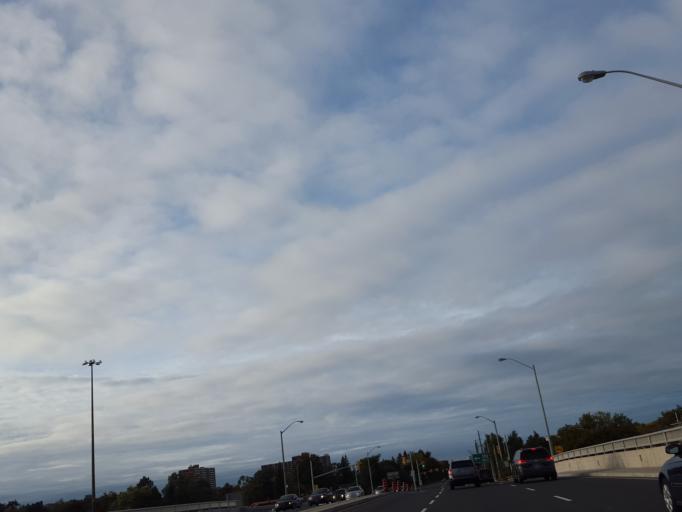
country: CA
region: Ontario
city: Scarborough
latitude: 43.7704
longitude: -79.3040
